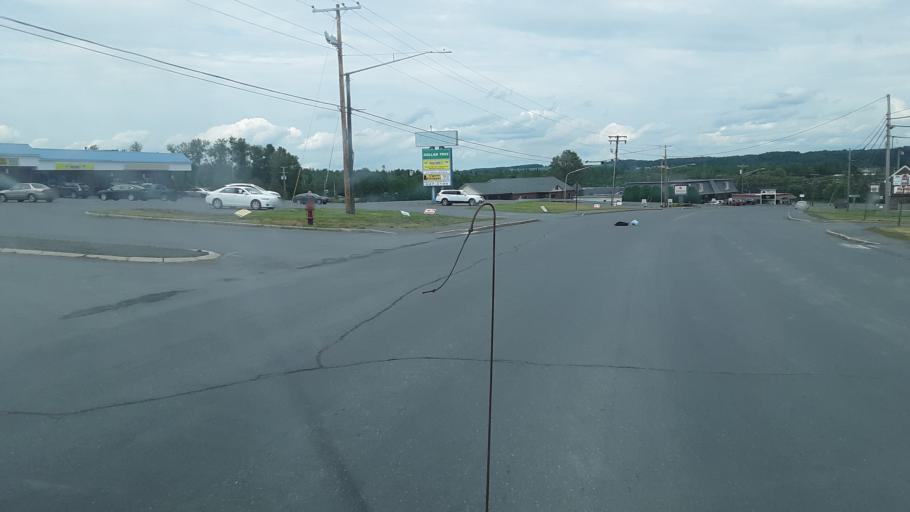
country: US
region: Maine
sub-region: Aroostook County
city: Caribou
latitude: 46.8692
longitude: -68.0040
